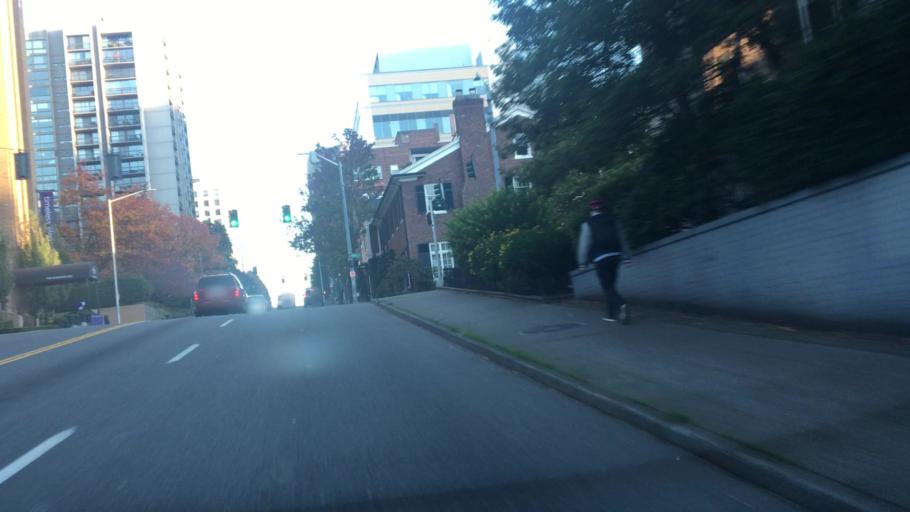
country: US
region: Washington
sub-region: King County
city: Seattle
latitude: 47.6118
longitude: -122.3275
